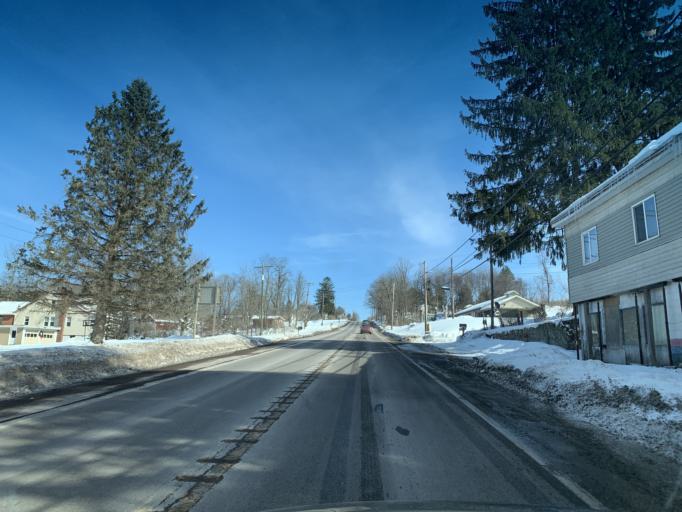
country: US
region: Pennsylvania
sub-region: Somerset County
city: Meyersdale
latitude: 39.6964
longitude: -79.1372
